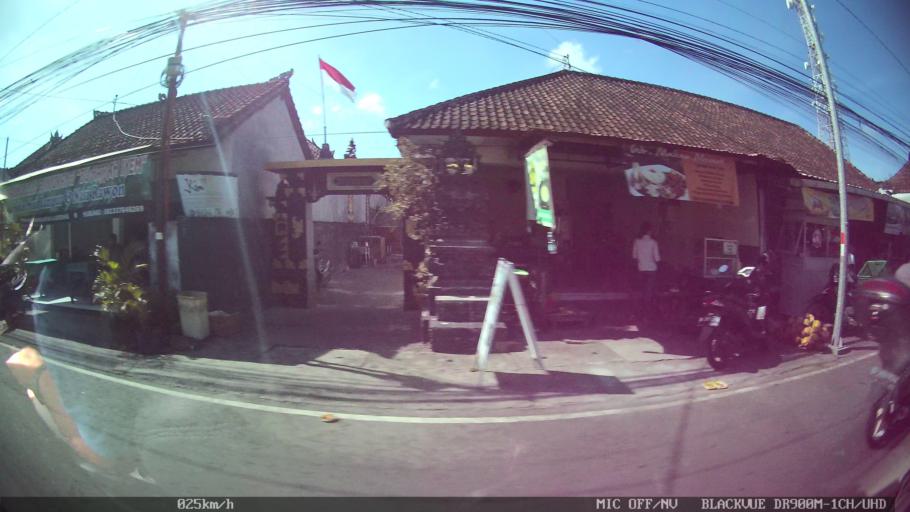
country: ID
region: Bali
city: Kuta
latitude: -8.7146
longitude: 115.1848
